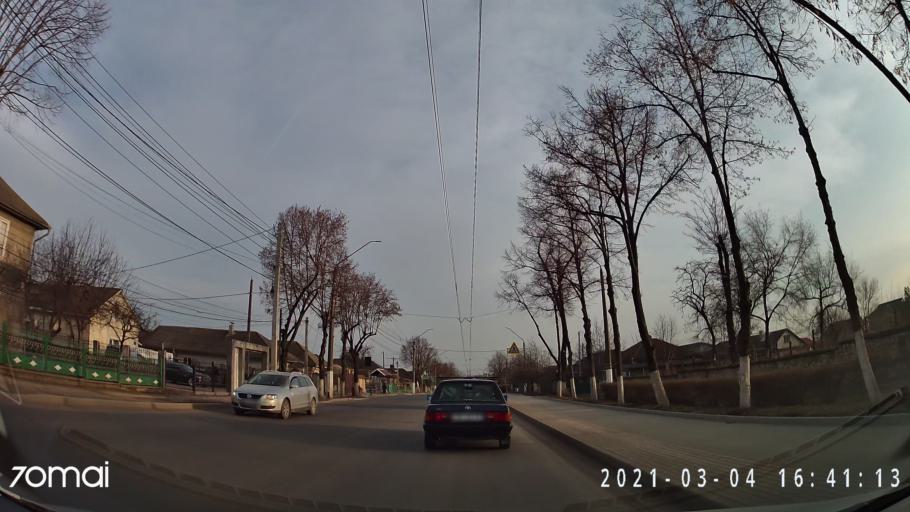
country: MD
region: Balti
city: Balti
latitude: 47.7702
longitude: 27.9007
